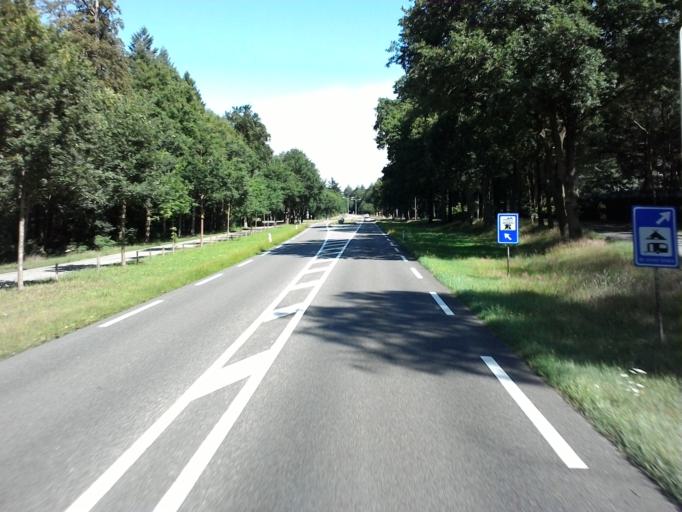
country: NL
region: Utrecht
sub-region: Gemeente Baarn
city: Baarn
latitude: 52.2018
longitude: 5.2502
